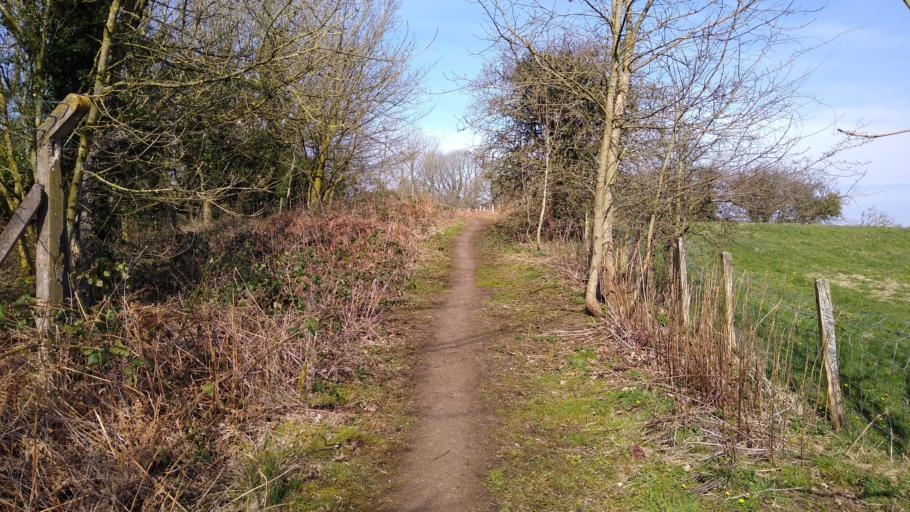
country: GB
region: England
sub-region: Cumbria
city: Dearham
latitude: 54.6740
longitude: -3.4145
